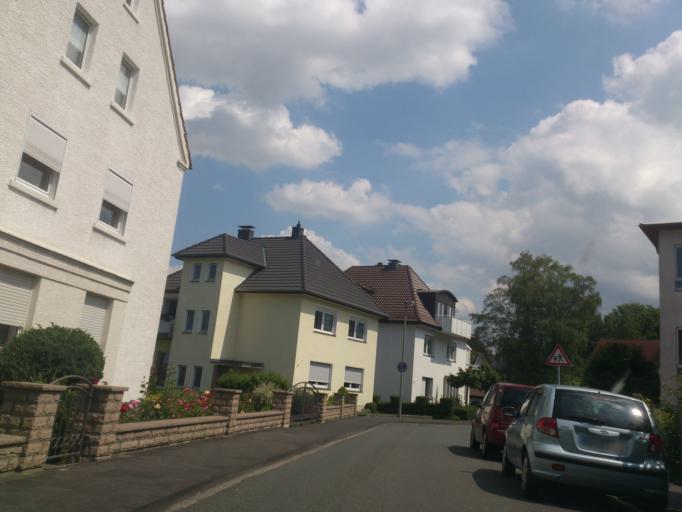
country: DE
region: North Rhine-Westphalia
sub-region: Regierungsbezirk Detmold
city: Paderborn
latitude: 51.7149
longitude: 8.7662
